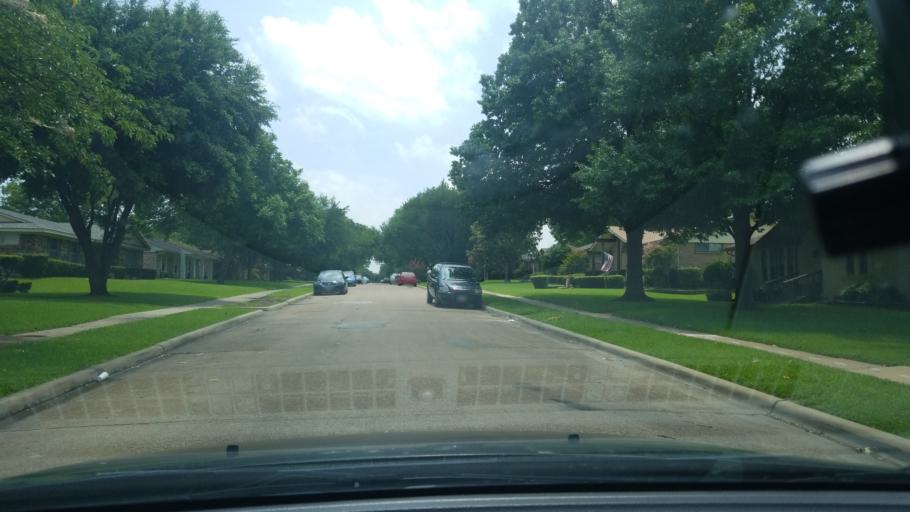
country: US
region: Texas
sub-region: Dallas County
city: Mesquite
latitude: 32.8040
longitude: -96.6372
